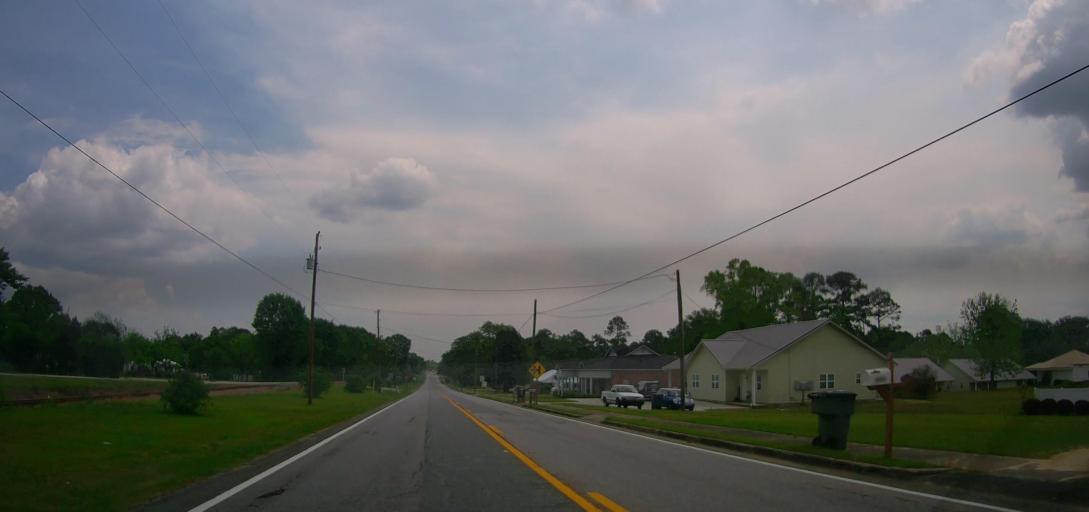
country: US
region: Georgia
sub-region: Treutlen County
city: Soperton
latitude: 32.3828
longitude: -82.5995
